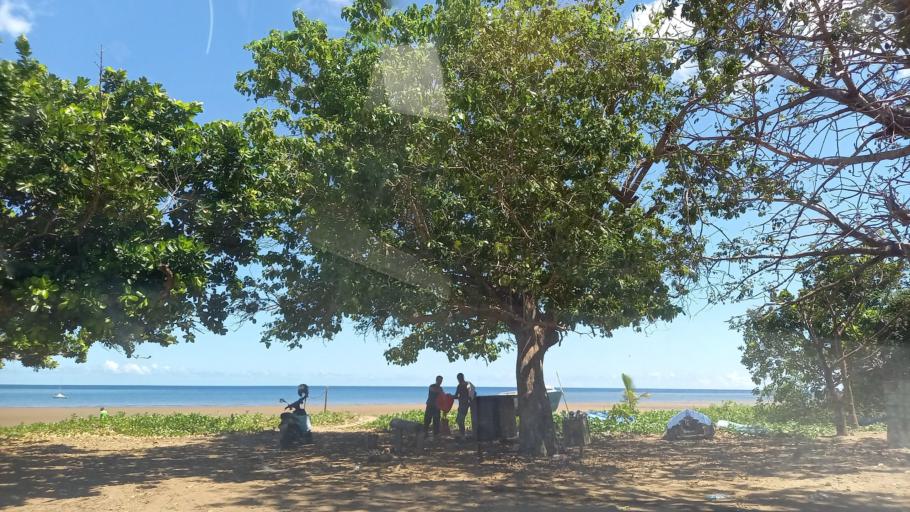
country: YT
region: Boueni
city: Boueni
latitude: -12.9239
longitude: 45.0885
